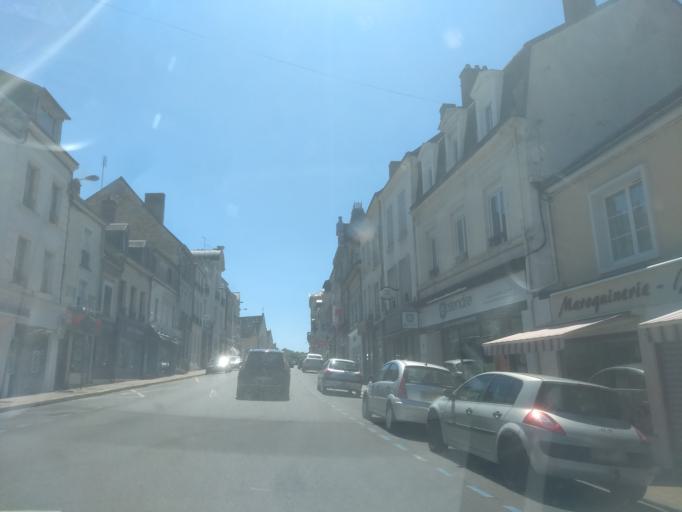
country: FR
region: Centre
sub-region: Departement d'Eure-et-Loir
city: Nogent-le-Rotrou
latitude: 48.3229
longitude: 0.8222
